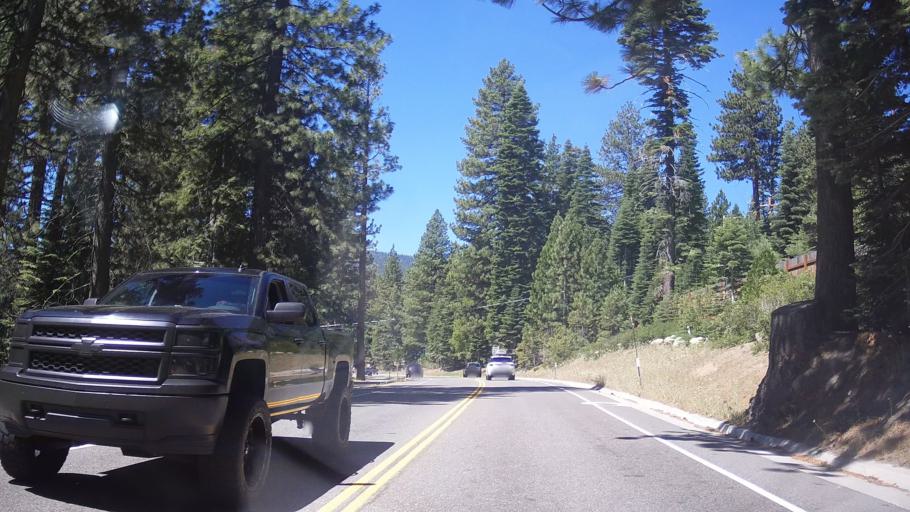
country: US
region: California
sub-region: Placer County
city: Sunnyside-Tahoe City
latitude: 39.1465
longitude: -120.1503
